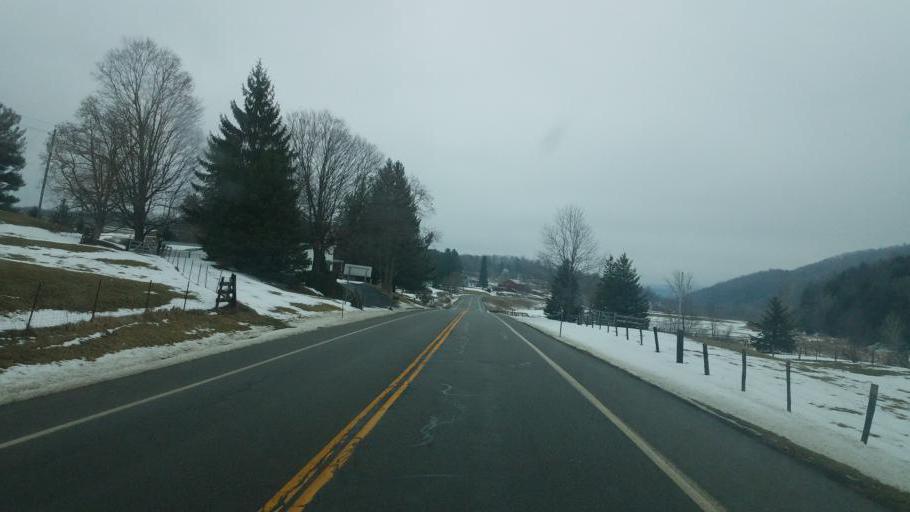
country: US
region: Pennsylvania
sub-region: Tioga County
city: Westfield
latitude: 42.0353
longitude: -77.5416
